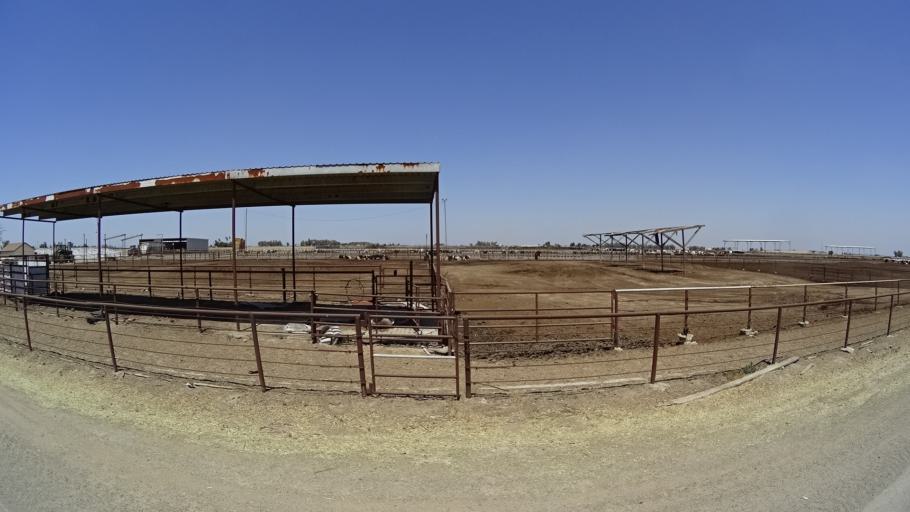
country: US
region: California
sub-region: Kings County
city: Home Garden
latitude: 36.1968
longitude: -119.6329
